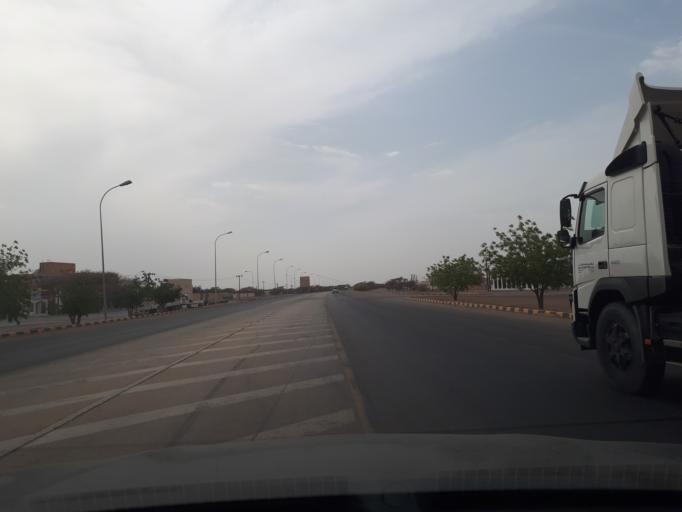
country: OM
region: Ash Sharqiyah
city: Badiyah
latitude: 22.4627
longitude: 58.7964
